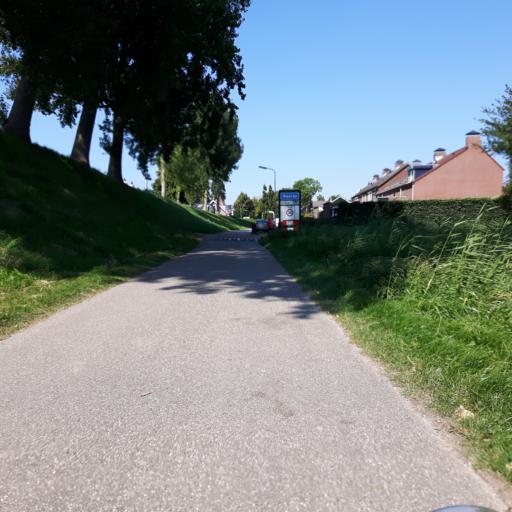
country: NL
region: Zeeland
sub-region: Gemeente Reimerswaal
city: Yerseke
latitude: 51.4149
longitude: 4.0665
